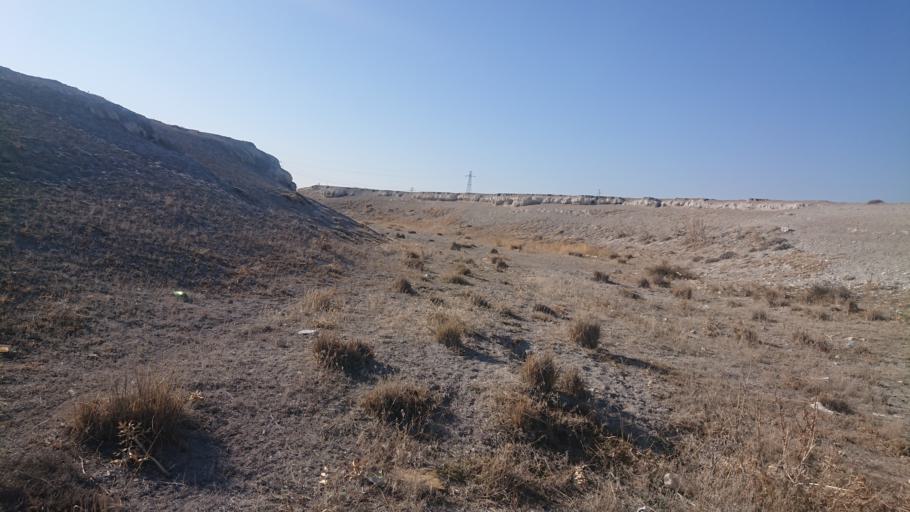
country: TR
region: Aksaray
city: Sultanhani
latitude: 38.2590
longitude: 33.5094
